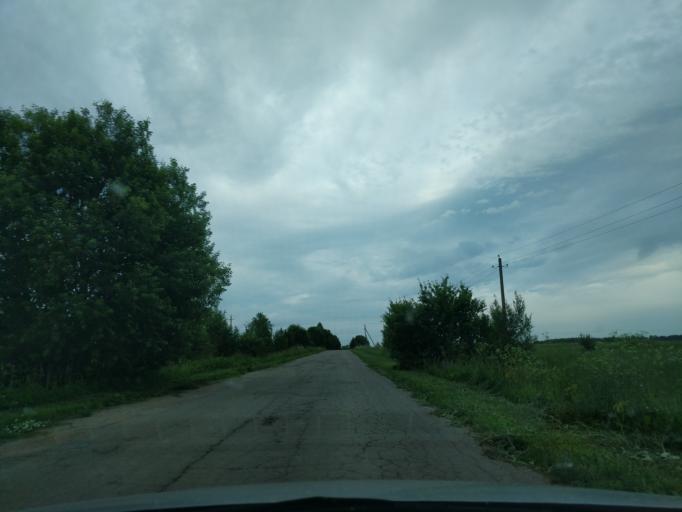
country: RU
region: Kaluga
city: Nikola-Lenivets
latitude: 54.7731
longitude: 35.7163
